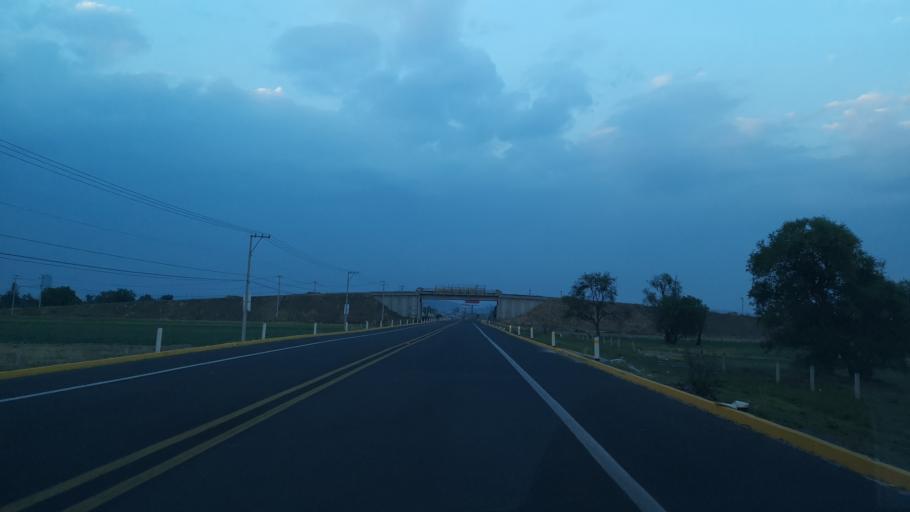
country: MX
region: Puebla
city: Santa Ana Xalmimilulco
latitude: 19.1922
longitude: -98.3670
